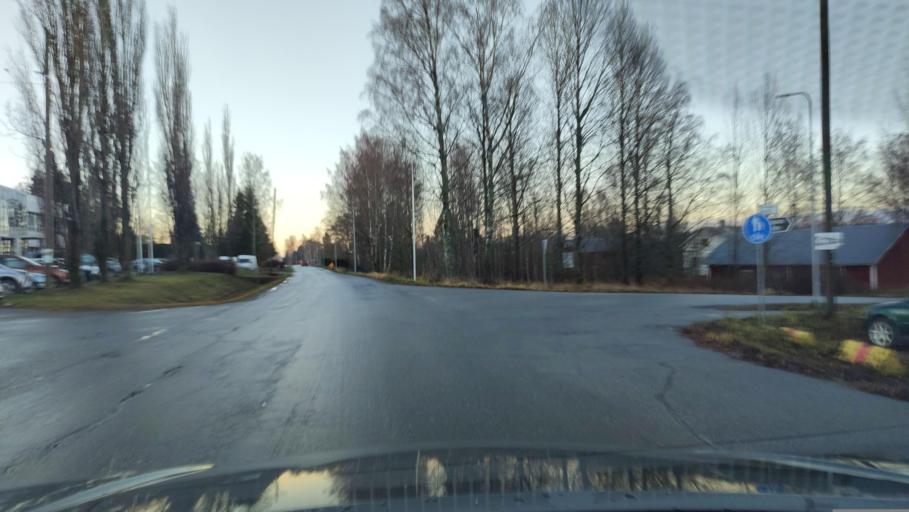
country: FI
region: Ostrobothnia
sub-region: Sydosterbotten
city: Naerpes
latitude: 62.4748
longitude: 21.3673
